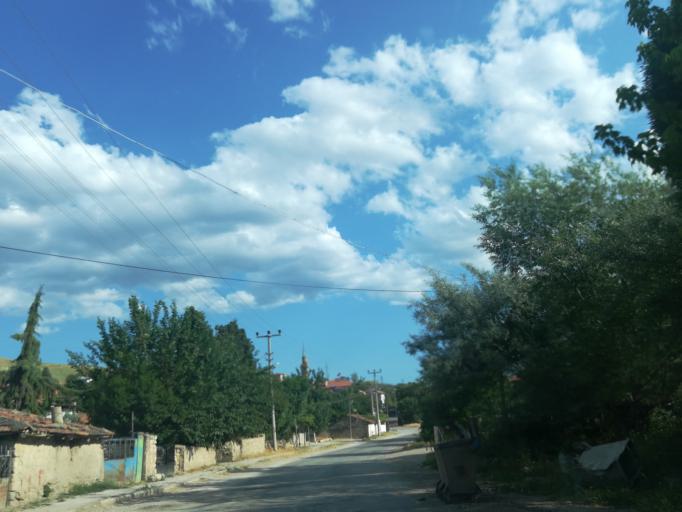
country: TR
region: Afyonkarahisar
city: Dinar
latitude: 38.0769
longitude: 30.1689
